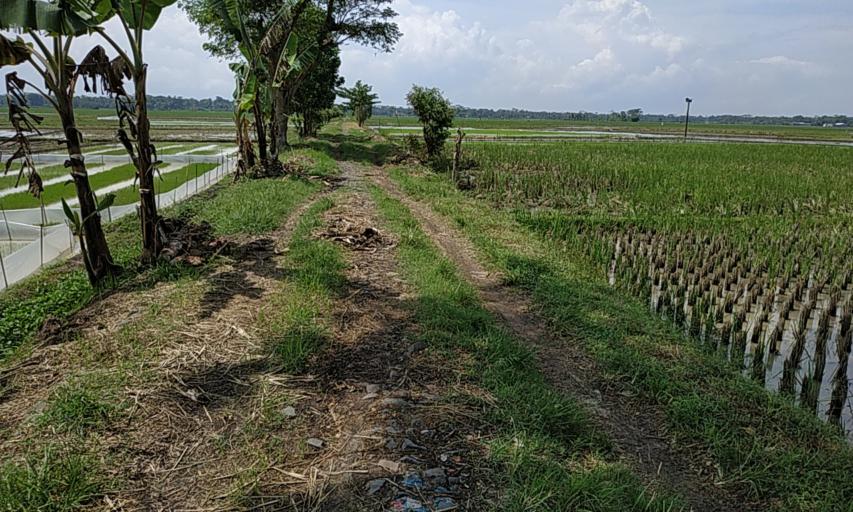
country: ID
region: Central Java
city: Kedungbulu
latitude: -7.5303
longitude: 108.7856
